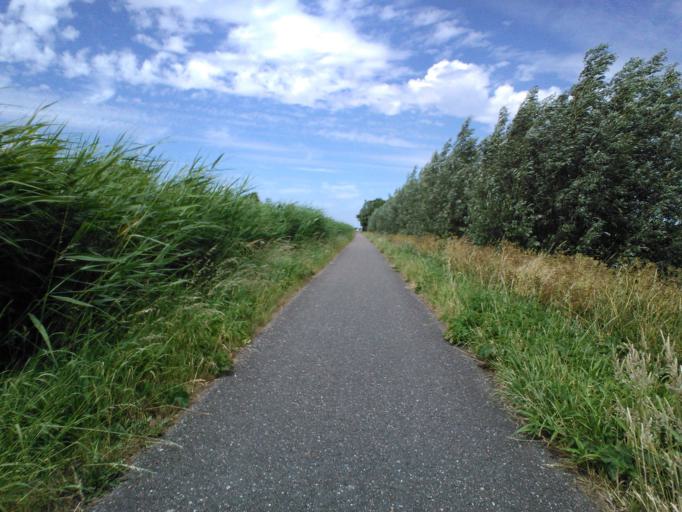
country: NL
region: South Holland
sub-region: Gemeente Giessenlanden
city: Giessenburg
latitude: 51.8632
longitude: 4.8815
